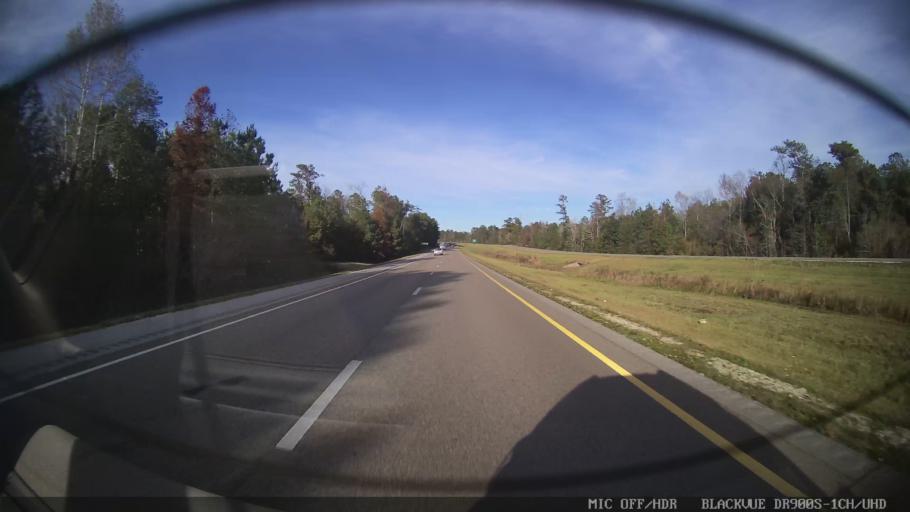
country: US
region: Mississippi
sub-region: Lamar County
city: West Hattiesburg
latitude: 31.2218
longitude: -89.3264
